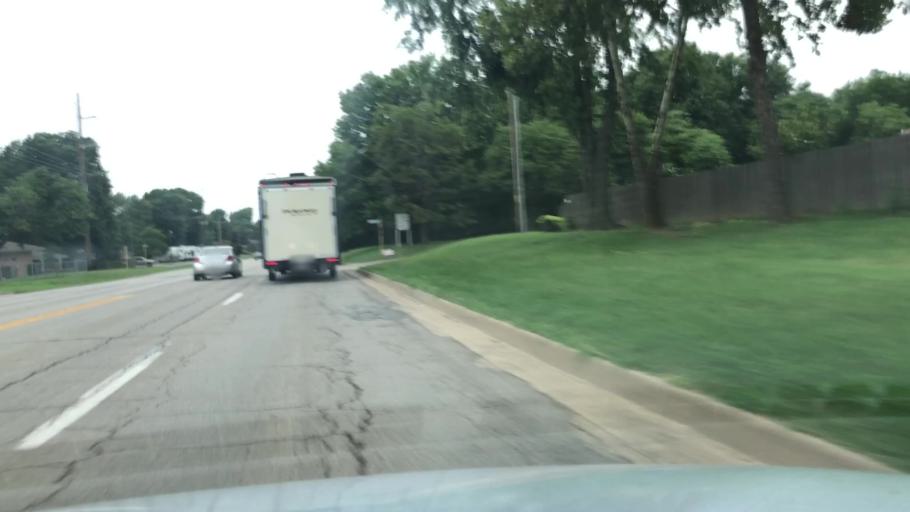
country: US
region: Oklahoma
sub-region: Washington County
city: Dewey
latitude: 36.7281
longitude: -95.9101
